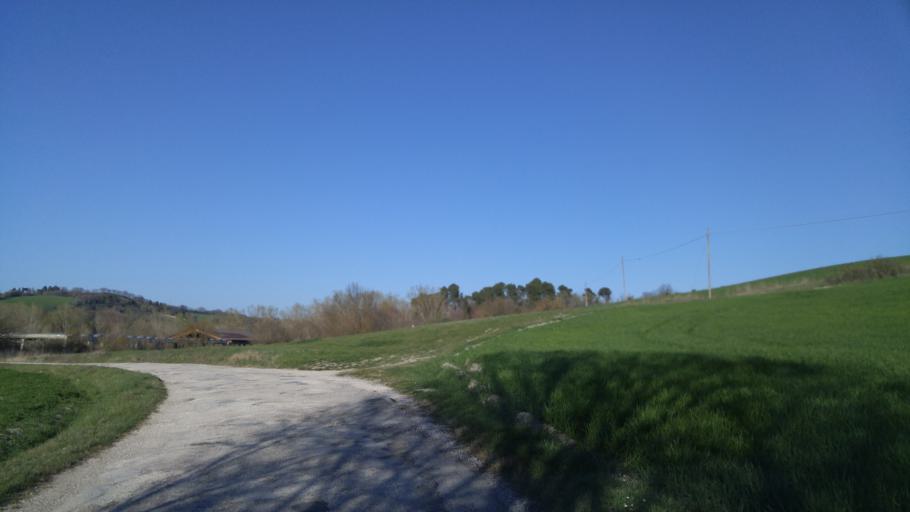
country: IT
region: The Marches
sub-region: Provincia di Pesaro e Urbino
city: Fenile
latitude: 43.8255
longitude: 12.9156
